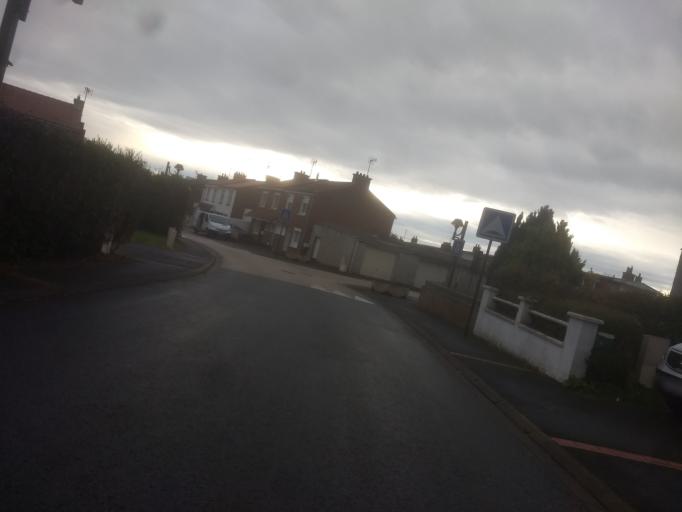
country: FR
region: Nord-Pas-de-Calais
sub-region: Departement du Pas-de-Calais
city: Dainville
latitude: 50.2881
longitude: 2.7406
